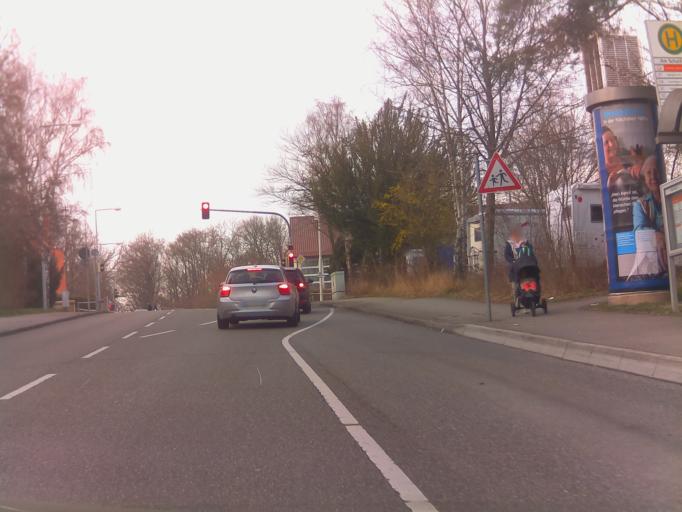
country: DE
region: Baden-Wuerttemberg
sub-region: Regierungsbezirk Stuttgart
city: Gerlingen
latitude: 48.7509
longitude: 9.0838
